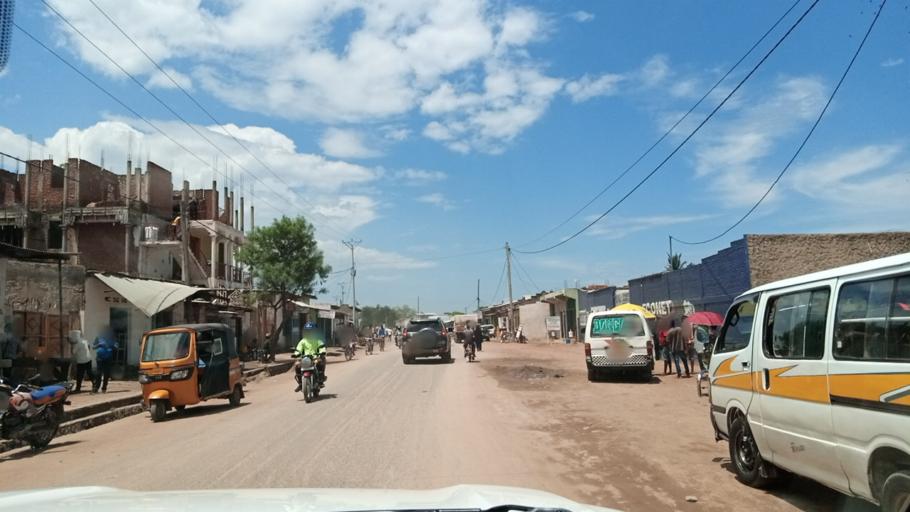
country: BI
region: Bujumbura Mairie
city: Bujumbura
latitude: -3.4272
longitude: 29.3550
